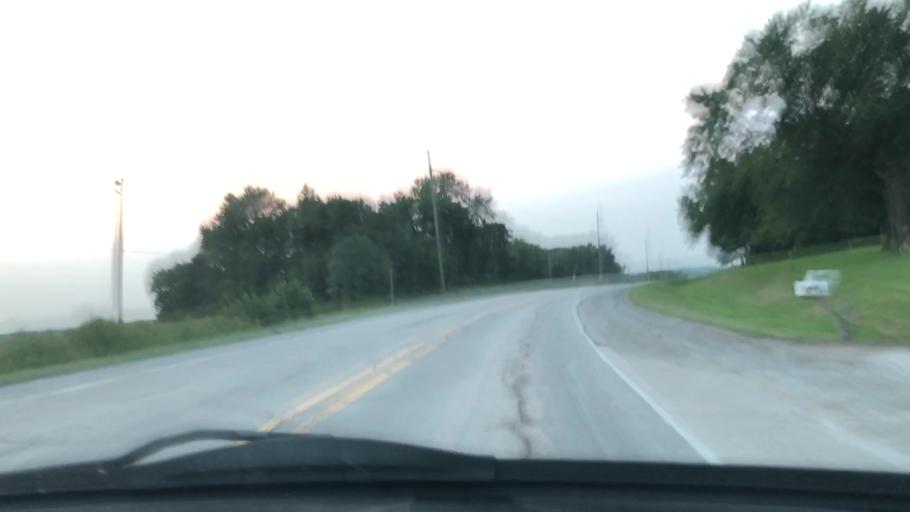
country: US
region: Iowa
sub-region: Johnson County
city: North Liberty
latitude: 41.7763
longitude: -91.6303
